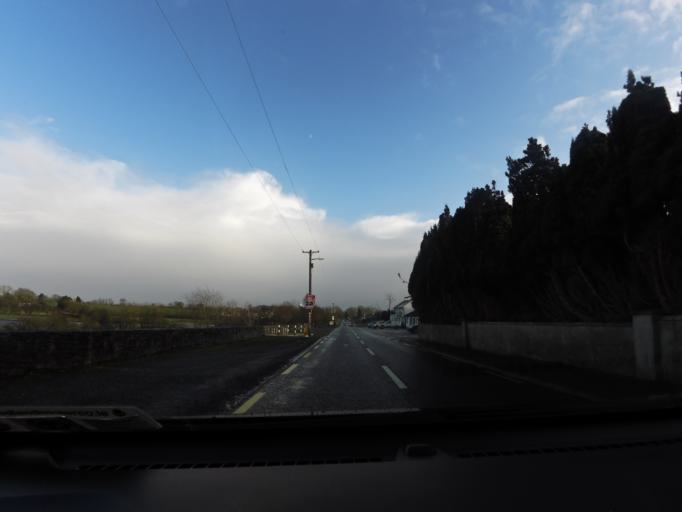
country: IE
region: Connaught
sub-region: County Galway
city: Tuam
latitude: 53.4916
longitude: -8.9362
